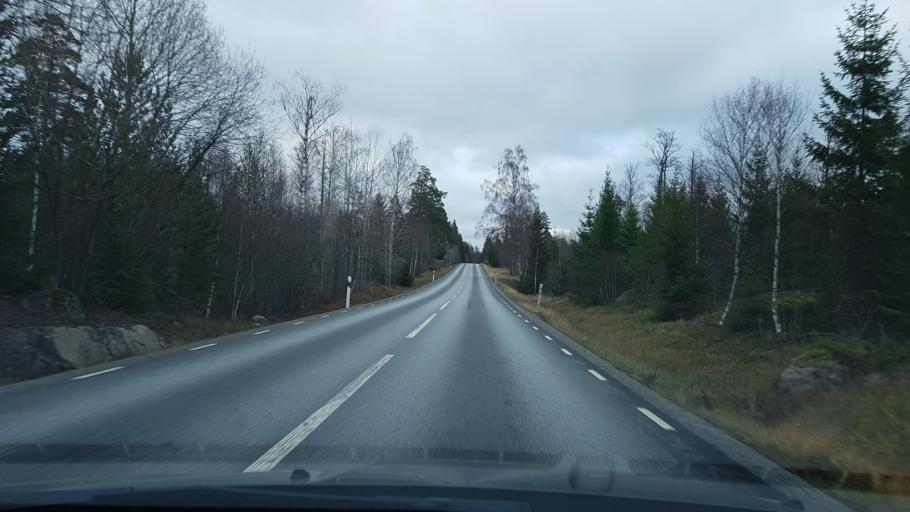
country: SE
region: Stockholm
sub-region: Norrtalje Kommun
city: Skanninge
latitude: 60.0365
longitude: 18.4830
